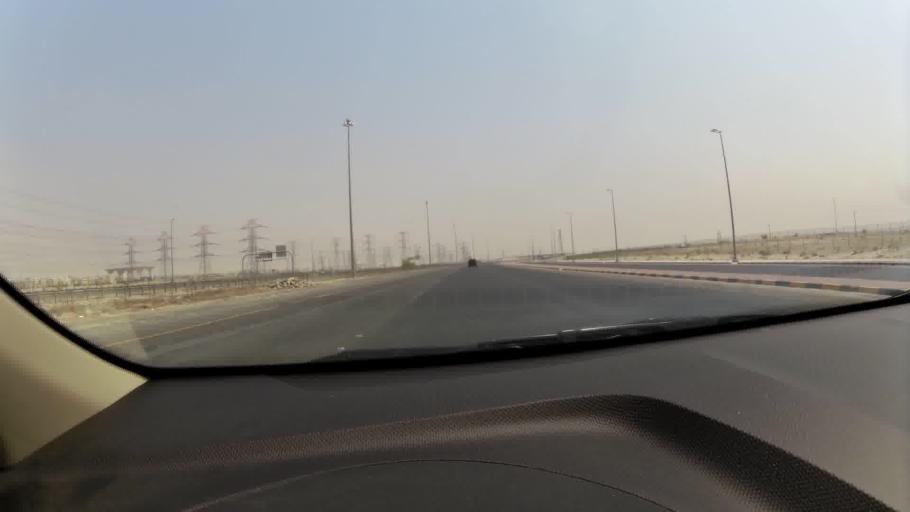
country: KW
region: Al Asimah
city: Ar Rabiyah
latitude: 29.2437
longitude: 47.8769
